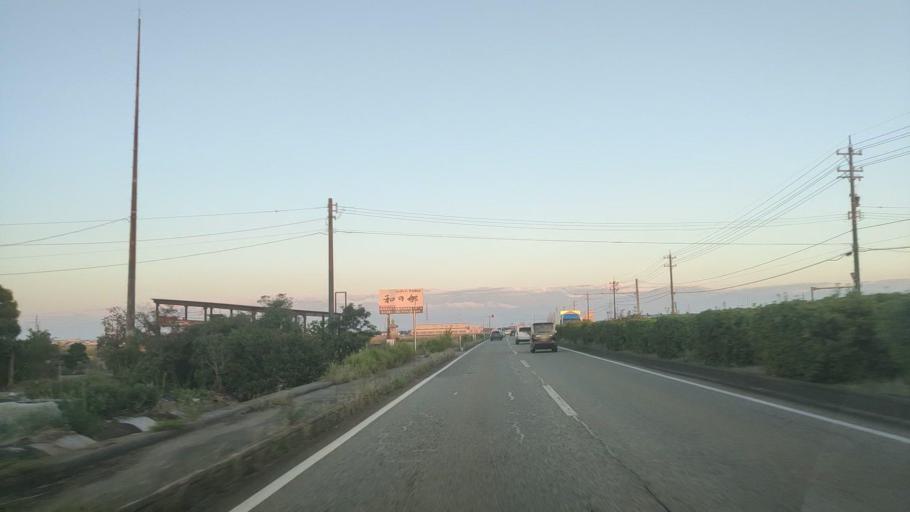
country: JP
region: Toyama
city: Nishishinminato
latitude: 36.7488
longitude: 137.0931
